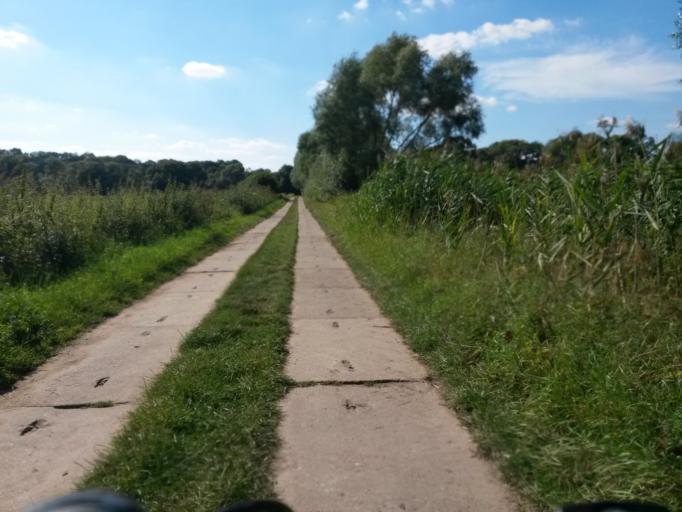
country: DE
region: Brandenburg
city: Schoneberg
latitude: 52.9495
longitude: 14.1174
